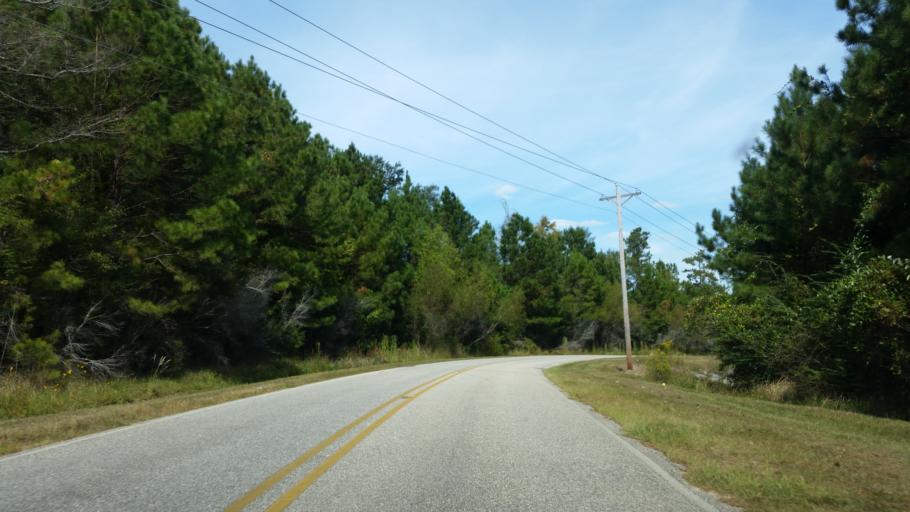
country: US
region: Alabama
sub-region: Baldwin County
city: Spanish Fort
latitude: 30.7445
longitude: -87.8910
